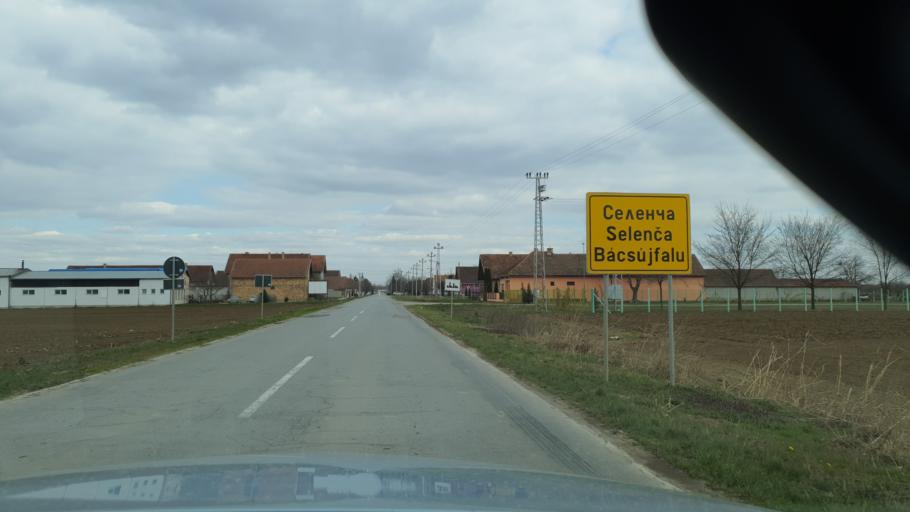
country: RS
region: Autonomna Pokrajina Vojvodina
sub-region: Juznobacki Okrug
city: Bac
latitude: 45.4017
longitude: 19.2817
